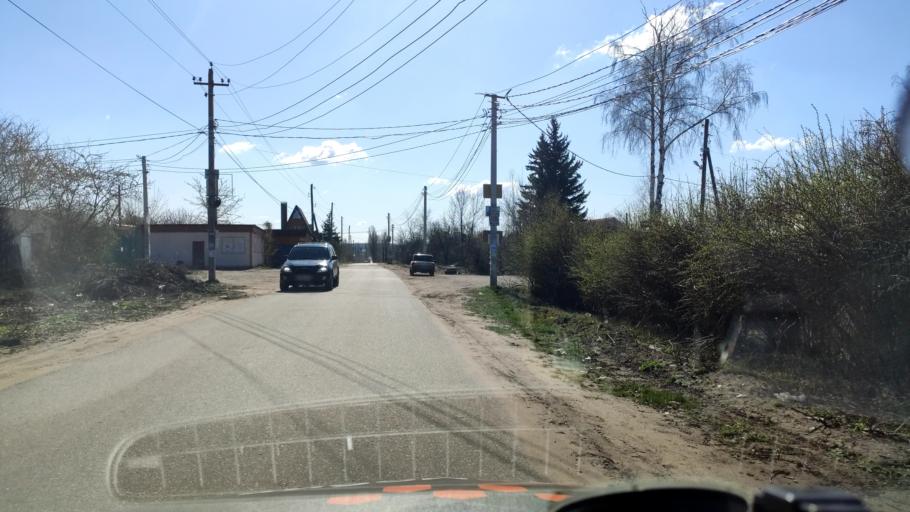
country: RU
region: Voronezj
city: Shilovo
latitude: 51.5996
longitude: 39.1447
